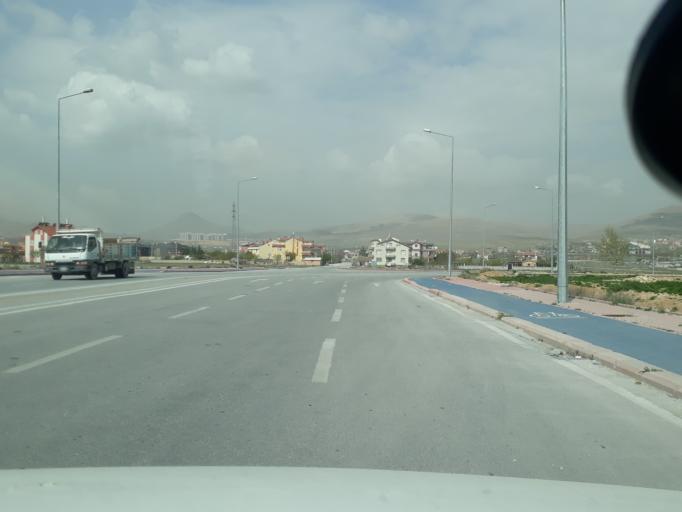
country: TR
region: Konya
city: Selcuklu
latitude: 37.9424
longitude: 32.4829
